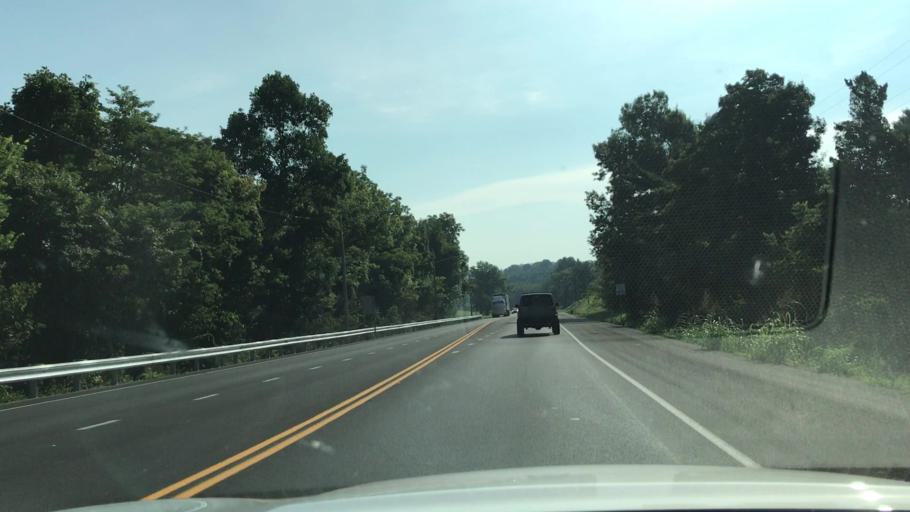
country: US
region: Kentucky
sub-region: Barren County
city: Glasgow
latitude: 37.0147
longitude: -85.9143
